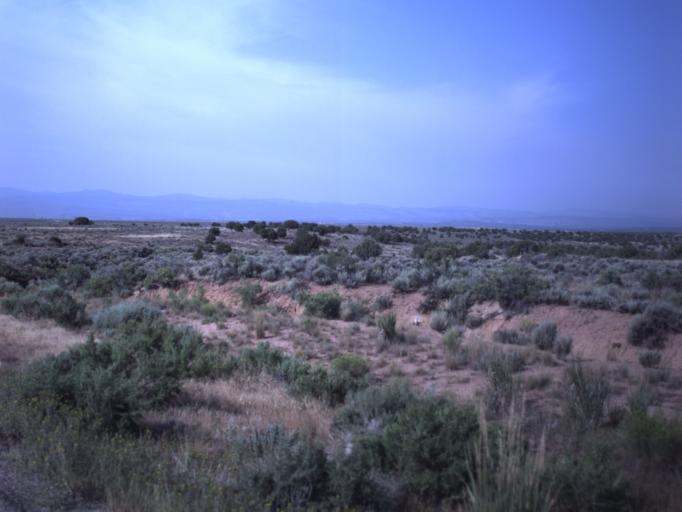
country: US
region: Utah
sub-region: Duchesne County
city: Duchesne
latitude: 40.2742
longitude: -110.3801
